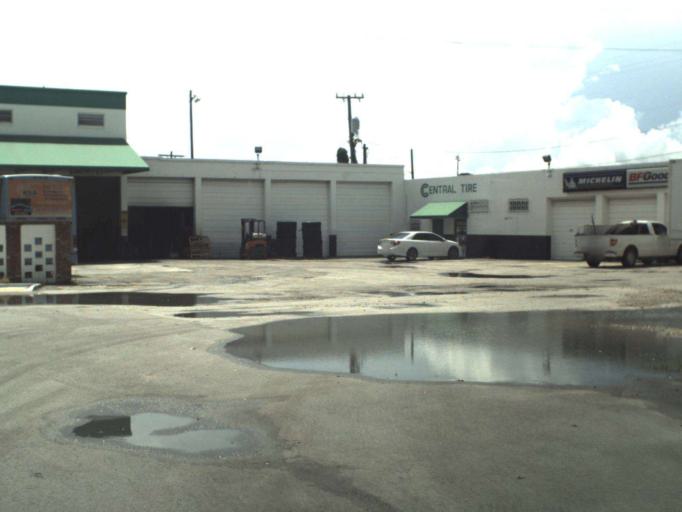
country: US
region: Florida
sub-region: Broward County
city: Fort Lauderdale
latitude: 26.0892
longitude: -80.1398
